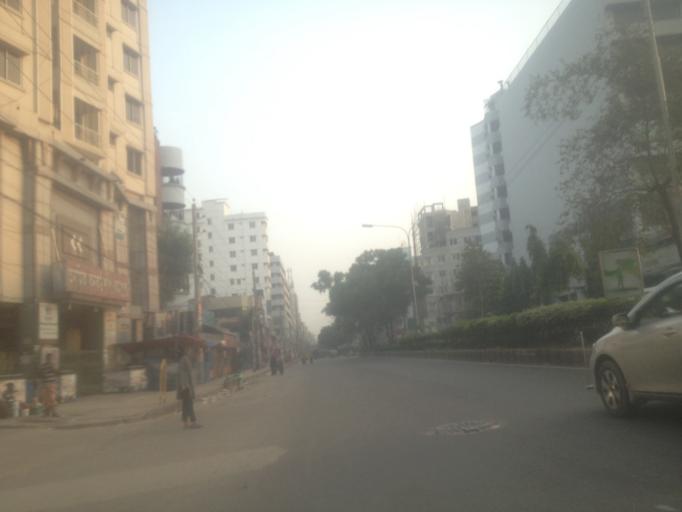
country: BD
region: Dhaka
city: Azimpur
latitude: 23.7879
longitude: 90.3768
